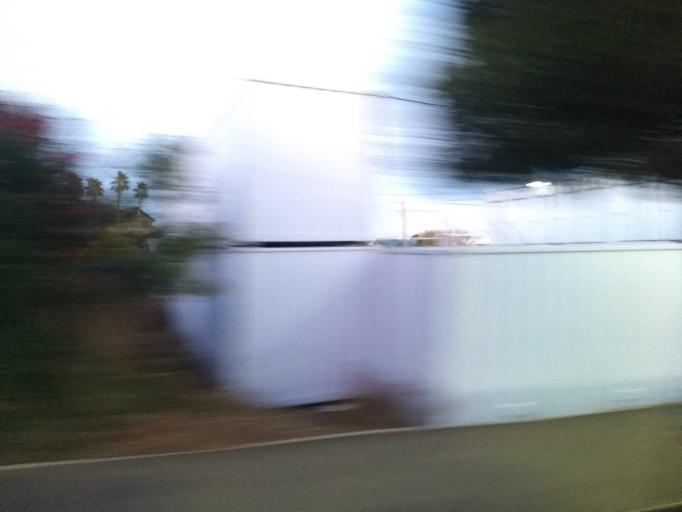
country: JP
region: Chiba
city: Kashiwa
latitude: 35.8706
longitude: 139.9520
